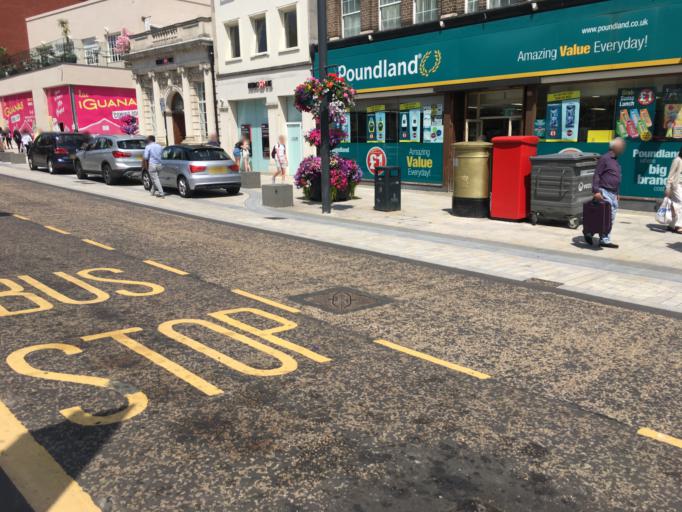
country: GB
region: England
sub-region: Hertfordshire
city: Watford
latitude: 51.6551
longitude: -0.3958
